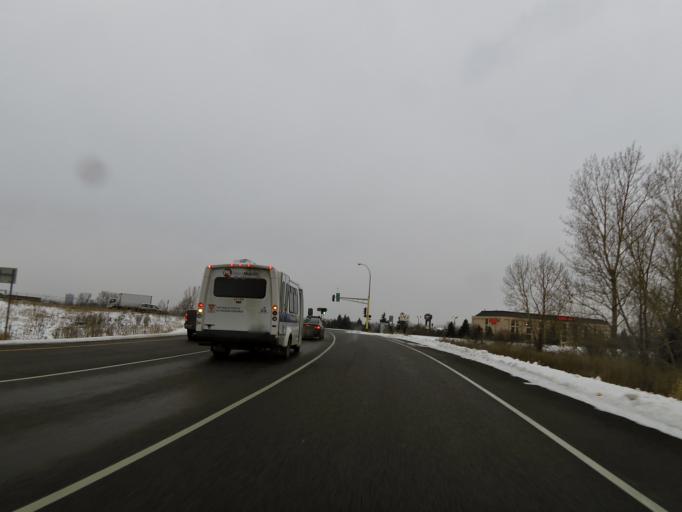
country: US
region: Minnesota
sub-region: Dakota County
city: Mendota Heights
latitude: 44.8488
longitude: -93.1544
